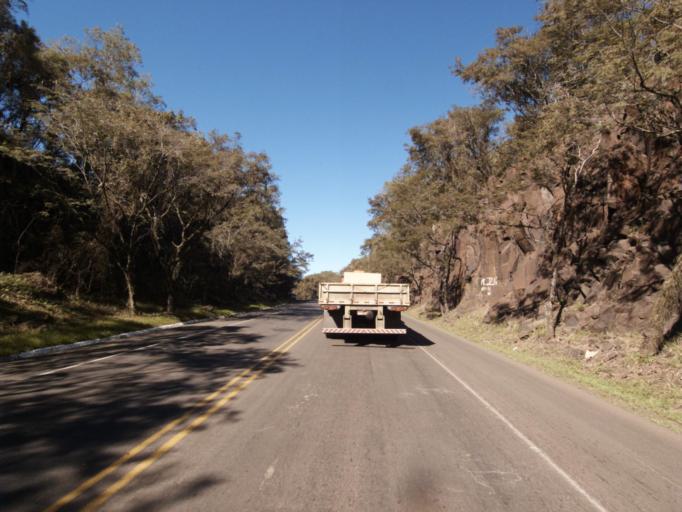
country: BR
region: Santa Catarina
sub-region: Chapeco
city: Chapeco
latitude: -26.9414
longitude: -52.7891
